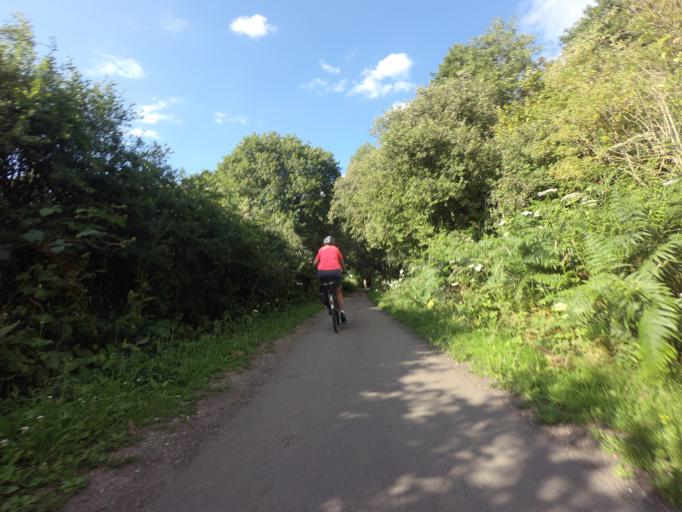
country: GB
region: England
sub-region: East Sussex
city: Hailsham
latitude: 50.8934
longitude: 0.2543
